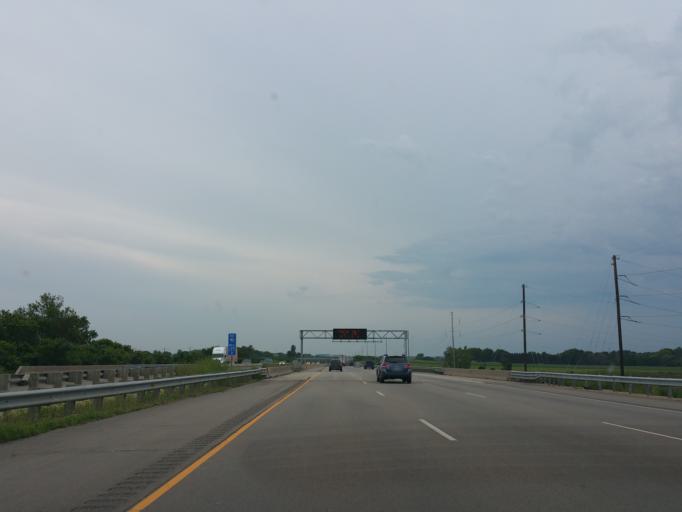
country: US
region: Wisconsin
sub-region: Dane County
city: Windsor
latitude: 43.2221
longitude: -89.3640
